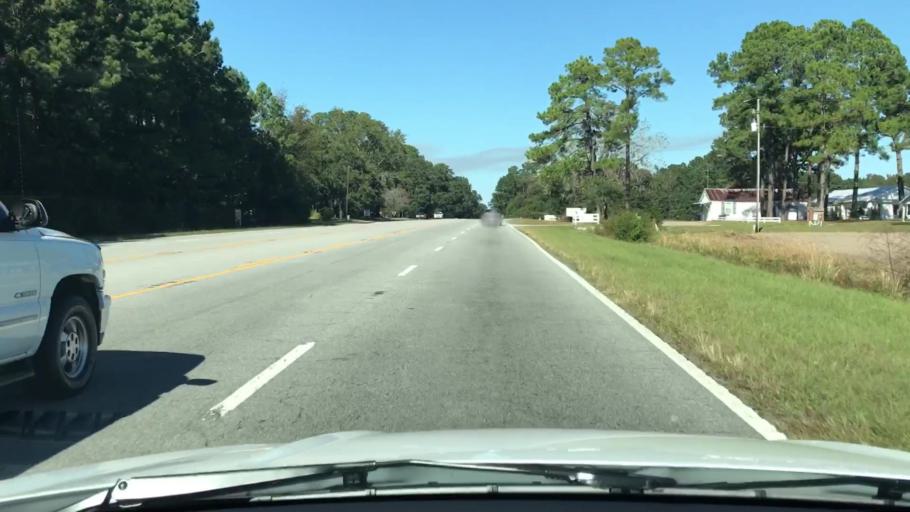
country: US
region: South Carolina
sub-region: Beaufort County
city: Laurel Bay
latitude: 32.5496
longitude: -80.7440
